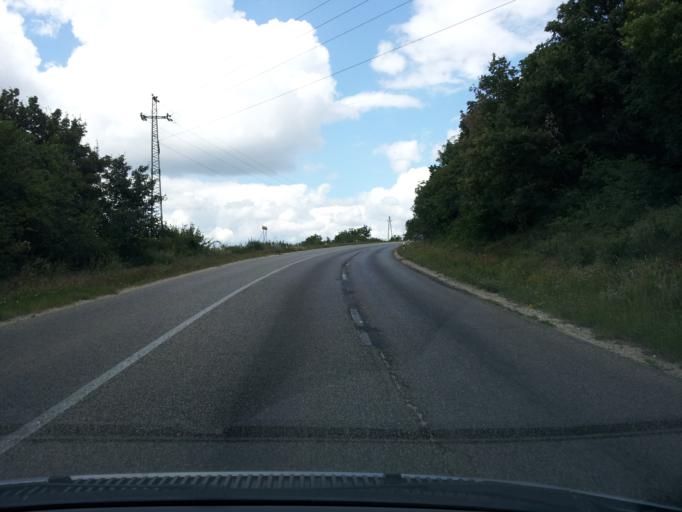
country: HU
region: Veszprem
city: Szentkiralyszabadja
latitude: 47.0558
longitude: 17.9934
